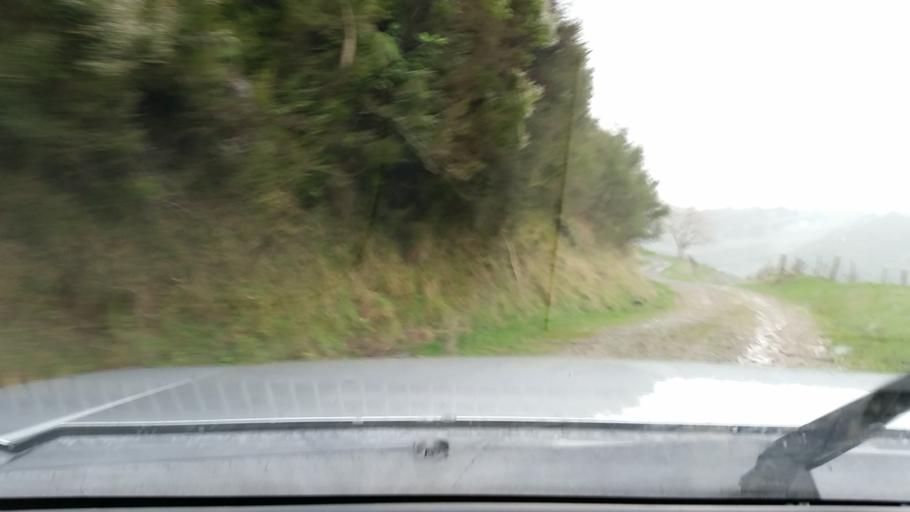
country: NZ
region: Waikato
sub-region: Otorohanga District
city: Otorohanga
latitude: -38.3839
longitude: 175.3881
